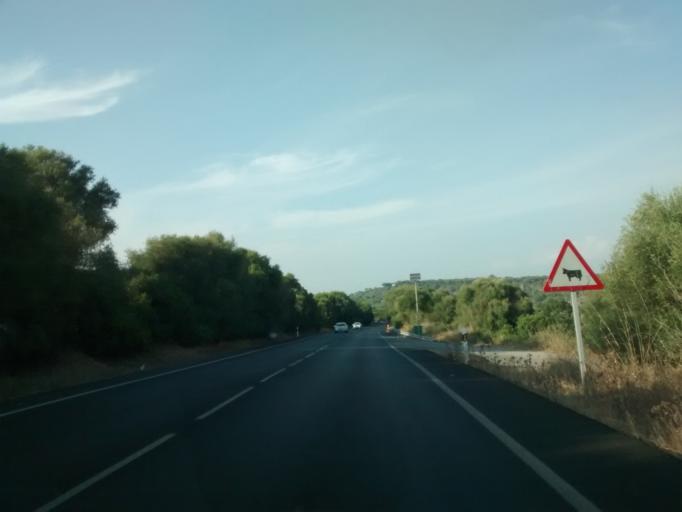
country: ES
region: Andalusia
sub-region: Provincia de Cadiz
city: Vejer de la Frontera
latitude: 36.2405
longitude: -5.9510
